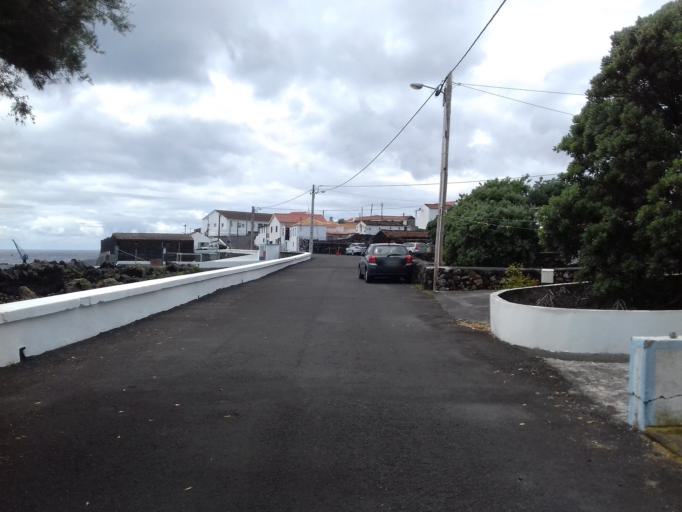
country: PT
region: Azores
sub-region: Sao Roque do Pico
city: Sao Roque do Pico
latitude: 38.4115
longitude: -28.0364
